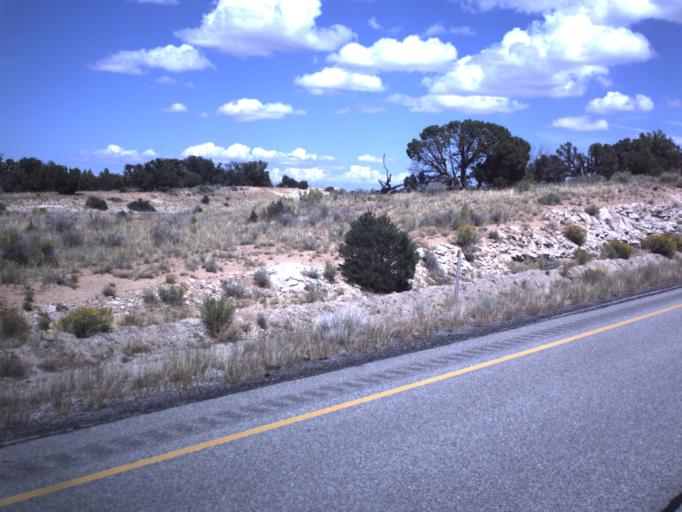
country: US
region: Utah
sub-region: Emery County
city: Ferron
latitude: 38.8469
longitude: -110.8898
